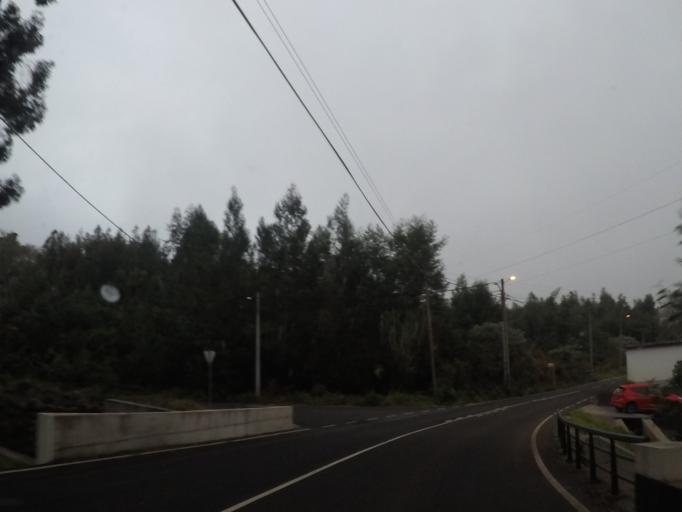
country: PT
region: Madeira
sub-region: Santa Cruz
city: Camacha
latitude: 32.7205
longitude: -16.8330
